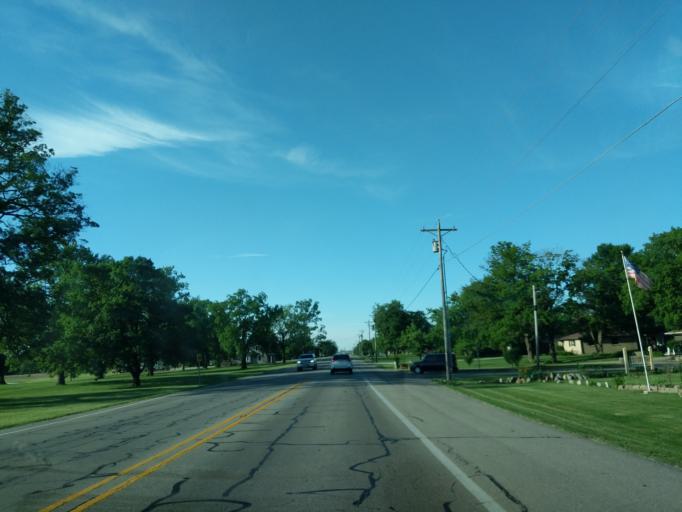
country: US
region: Indiana
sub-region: Hancock County
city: Greenfield
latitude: 39.8380
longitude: -85.7700
